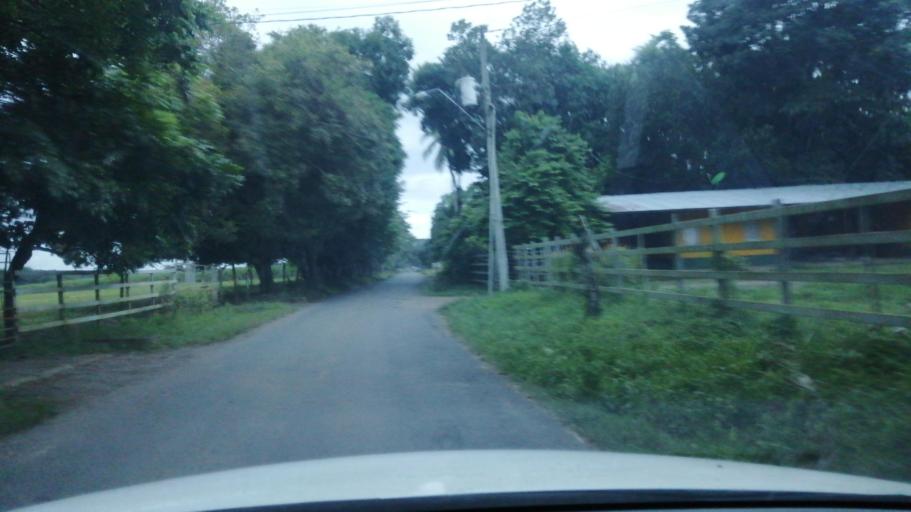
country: PA
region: Chiriqui
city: Alanje
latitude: 8.4016
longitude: -82.4988
